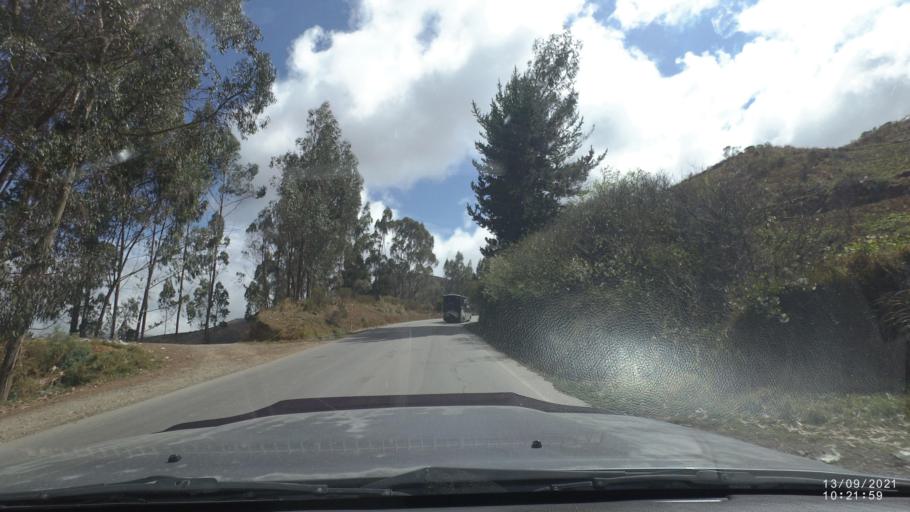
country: BO
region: Cochabamba
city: Colomi
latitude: -17.3183
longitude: -65.8738
